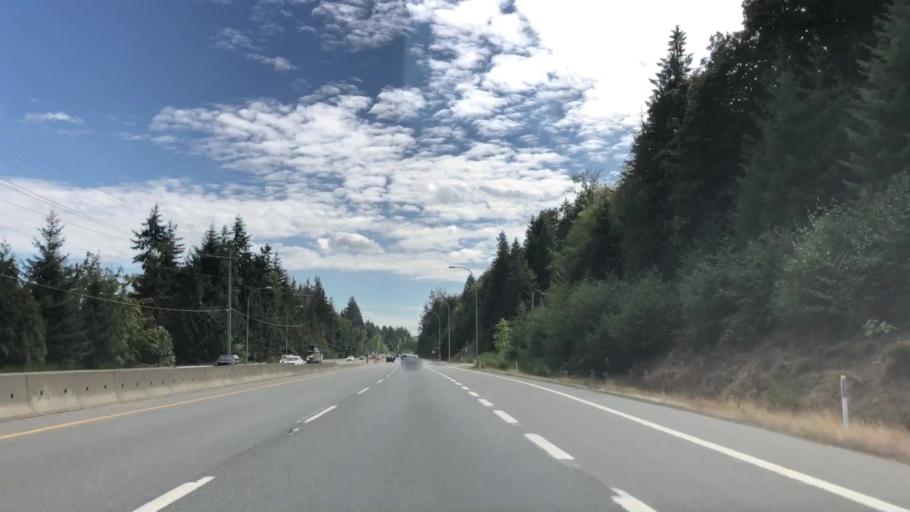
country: CA
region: British Columbia
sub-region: Cowichan Valley Regional District
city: Ladysmith
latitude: 48.9329
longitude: -123.7581
